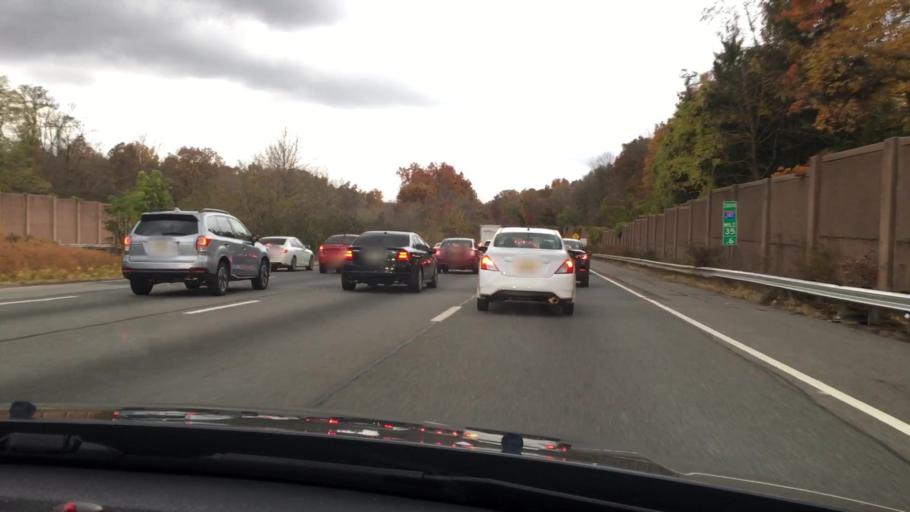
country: US
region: New Jersey
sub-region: Morris County
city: Morristown
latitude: 40.7834
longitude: -74.4717
